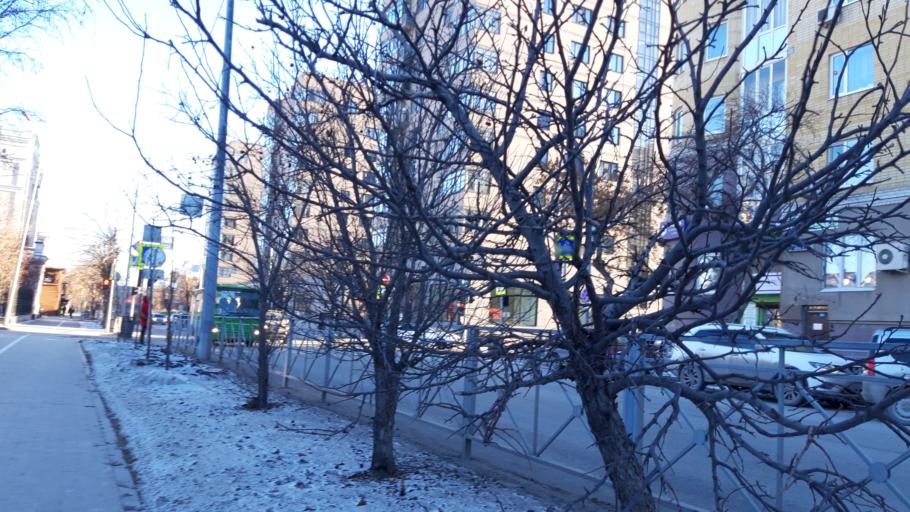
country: RU
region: Tjumen
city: Tyumen
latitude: 57.1598
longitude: 65.5445
